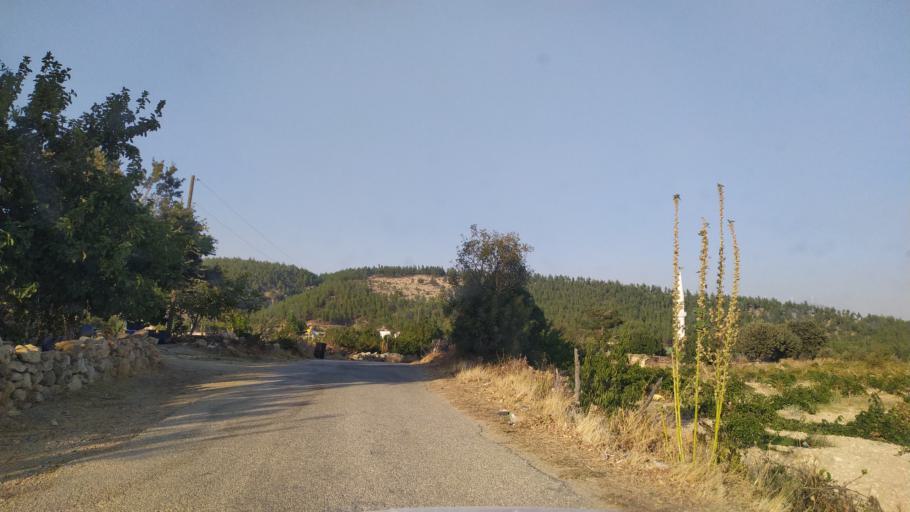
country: TR
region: Mersin
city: Mut
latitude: 36.6917
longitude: 33.1989
